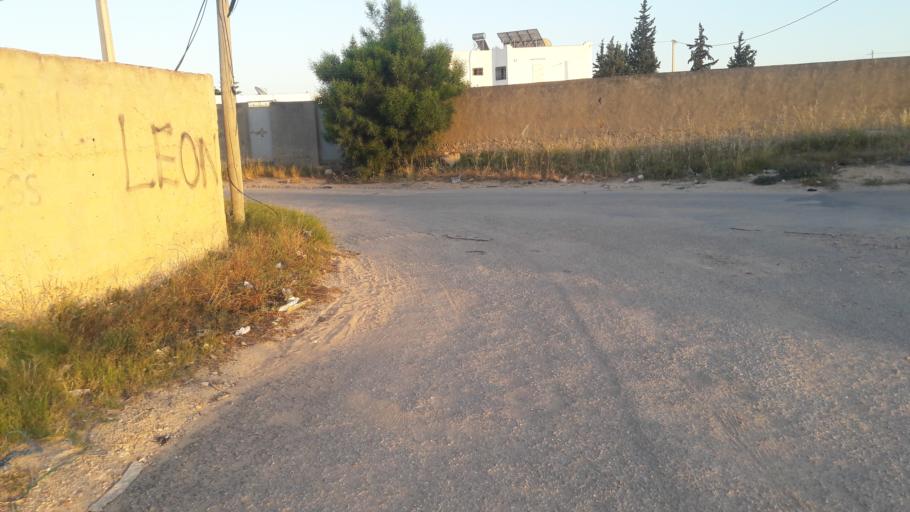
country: TN
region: Safaqis
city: Sfax
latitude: 34.8084
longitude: 10.7443
